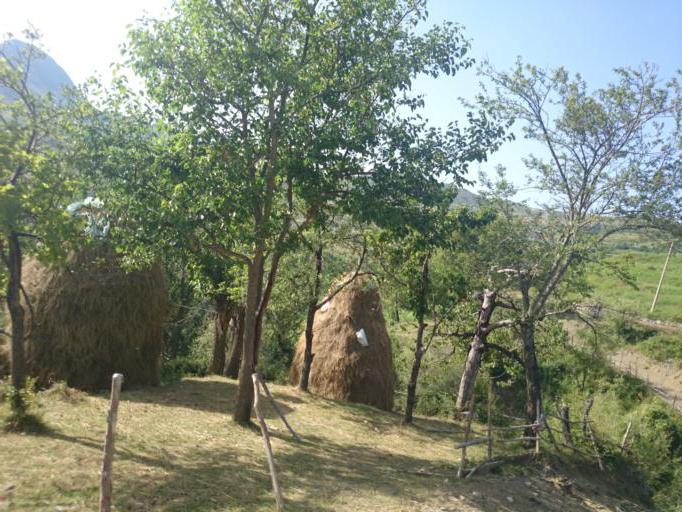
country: AL
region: Elbasan
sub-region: Rrethi i Gramshit
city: Lenias
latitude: 40.7805
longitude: 20.3895
